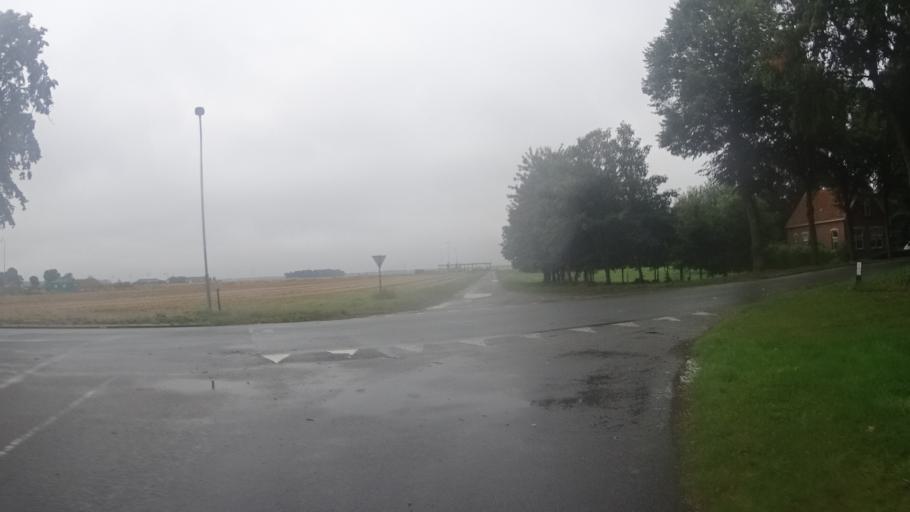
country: NL
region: Groningen
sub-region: Gemeente Veendam
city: Veendam
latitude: 53.1793
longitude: 6.8749
